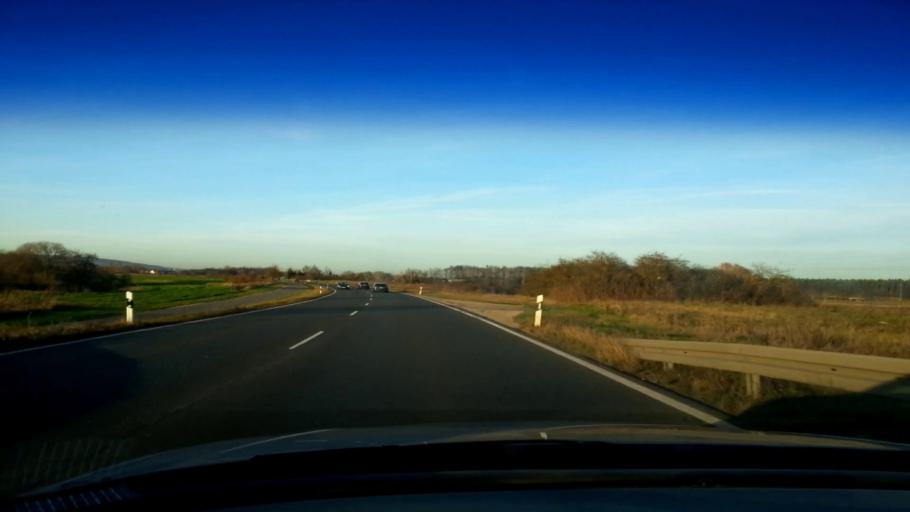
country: DE
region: Bavaria
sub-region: Upper Franconia
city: Hallstadt
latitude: 49.9408
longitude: 10.8841
